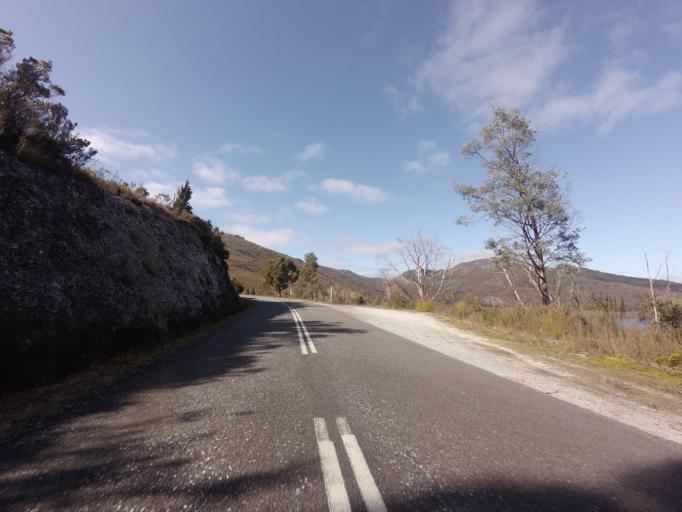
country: AU
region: Tasmania
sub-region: Huon Valley
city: Geeveston
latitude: -42.8490
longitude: 146.1742
